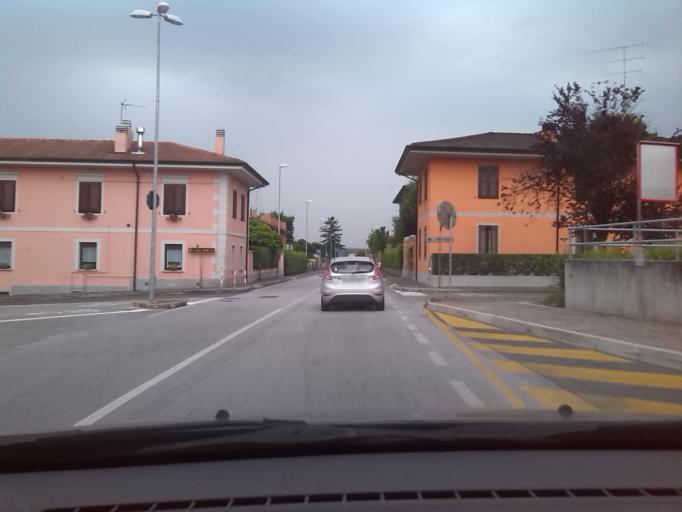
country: IT
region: Friuli Venezia Giulia
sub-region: Provincia di Udine
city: Majano
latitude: 46.1837
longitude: 13.0682
